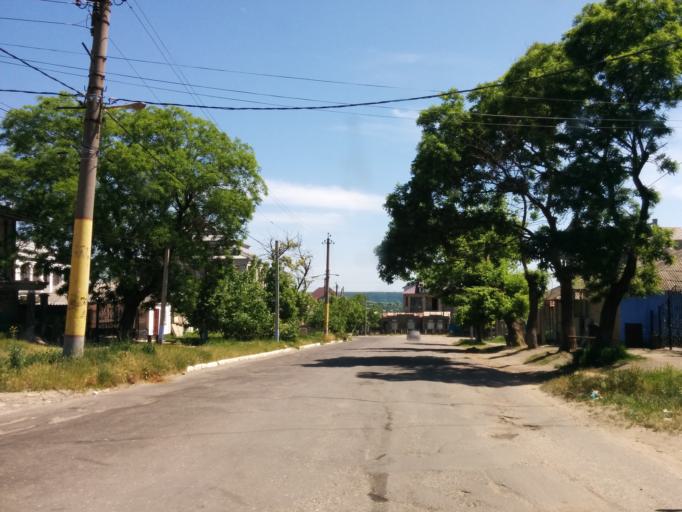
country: MD
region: Raionul Soroca
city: Soroca
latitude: 48.1609
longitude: 28.2930
